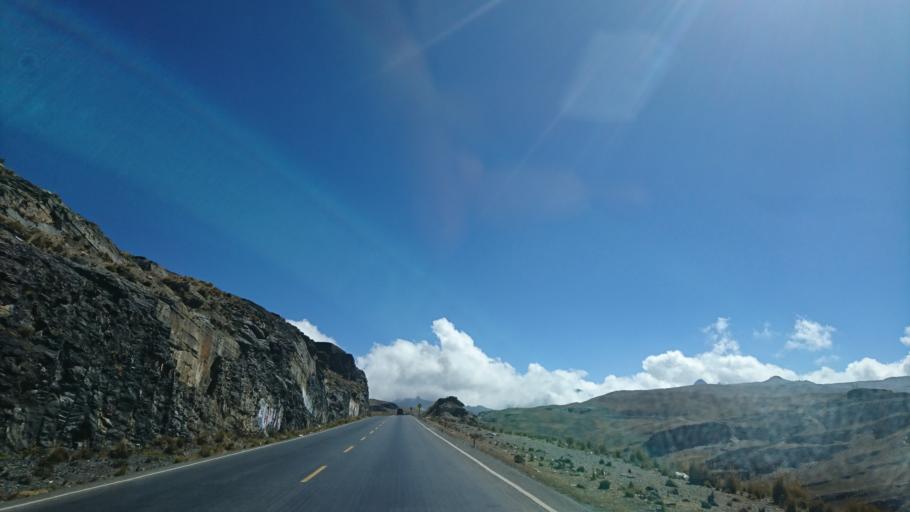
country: BO
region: La Paz
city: La Paz
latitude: -16.3774
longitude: -68.0447
